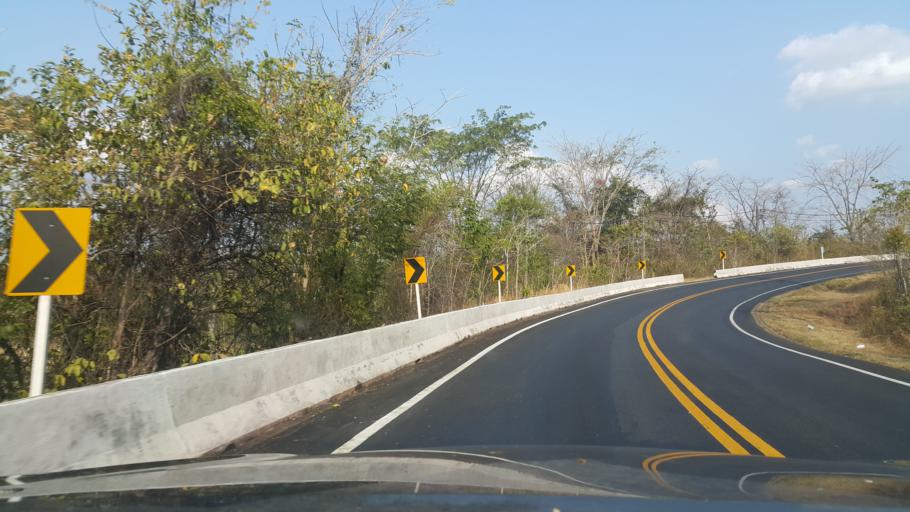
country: TH
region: Phitsanulok
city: Nakhon Thai
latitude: 17.1683
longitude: 100.9853
